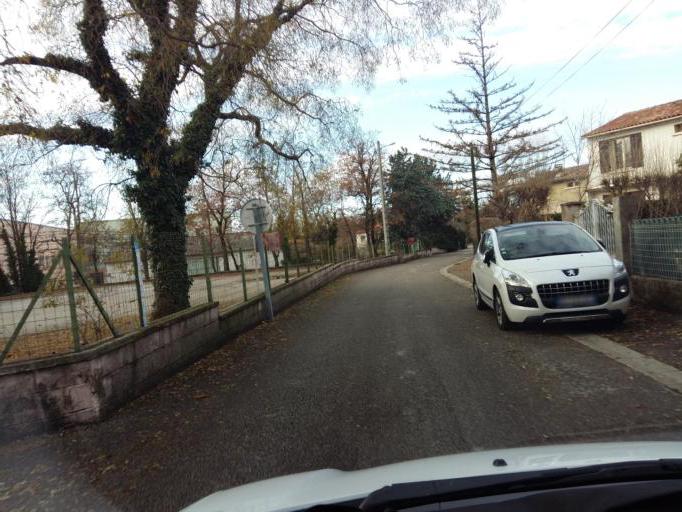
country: FR
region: Provence-Alpes-Cote d'Azur
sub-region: Departement du Vaucluse
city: Valreas
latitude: 44.3862
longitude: 4.9859
